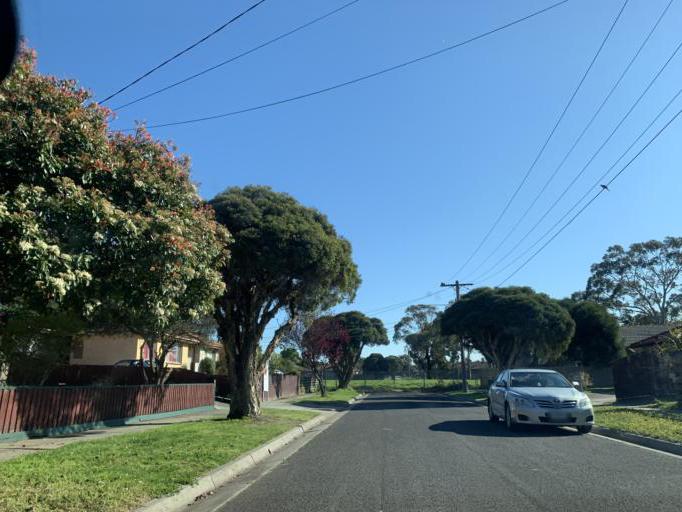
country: AU
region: Victoria
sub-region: Greater Dandenong
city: Dandenong
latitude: -37.9877
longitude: 145.1871
